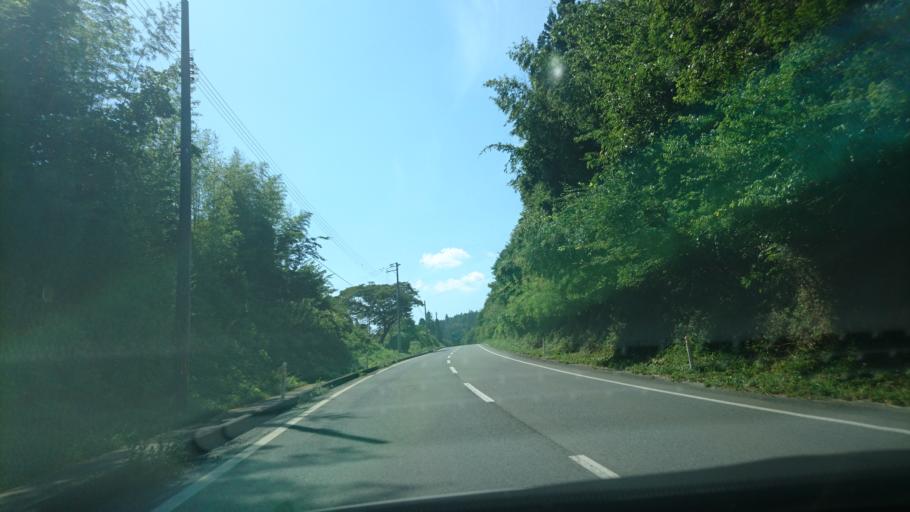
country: JP
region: Iwate
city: Ofunato
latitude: 39.0253
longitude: 141.5839
